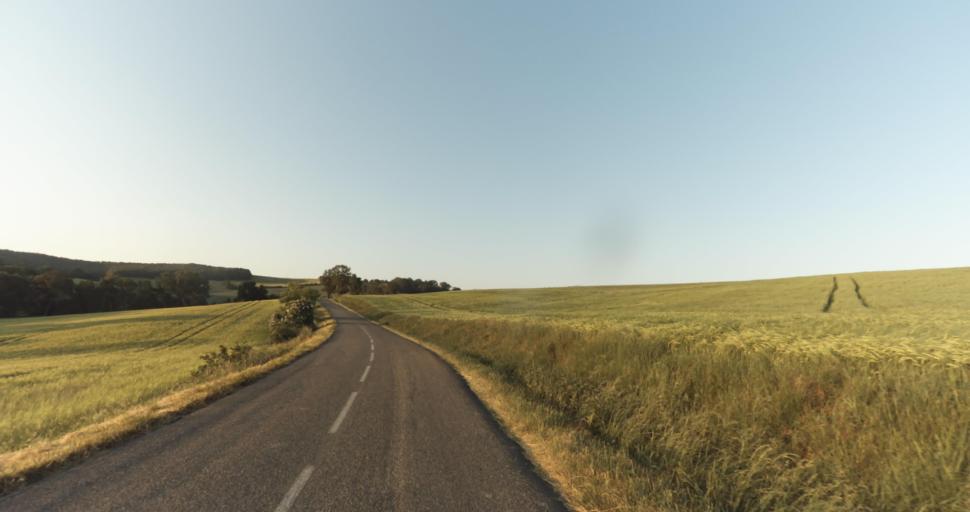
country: FR
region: Midi-Pyrenees
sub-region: Departement du Gers
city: Pujaudran
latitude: 43.6204
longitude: 1.1560
